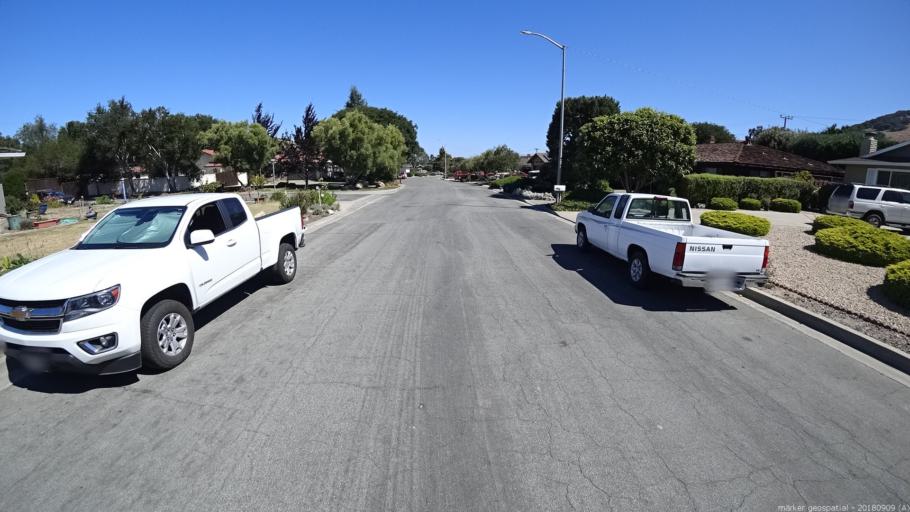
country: US
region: California
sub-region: Monterey County
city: Salinas
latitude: 36.6093
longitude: -121.6949
